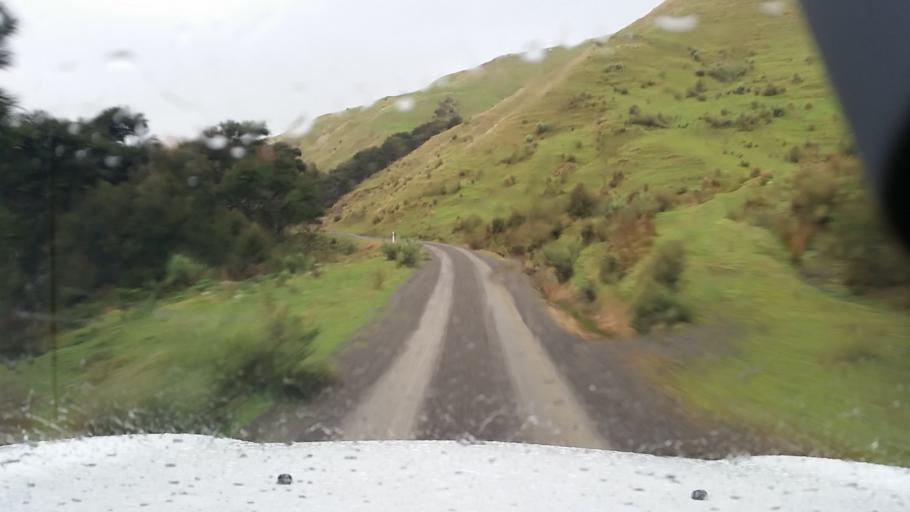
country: NZ
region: Wellington
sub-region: South Wairarapa District
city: Waipawa
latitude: -41.3691
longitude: 175.7057
